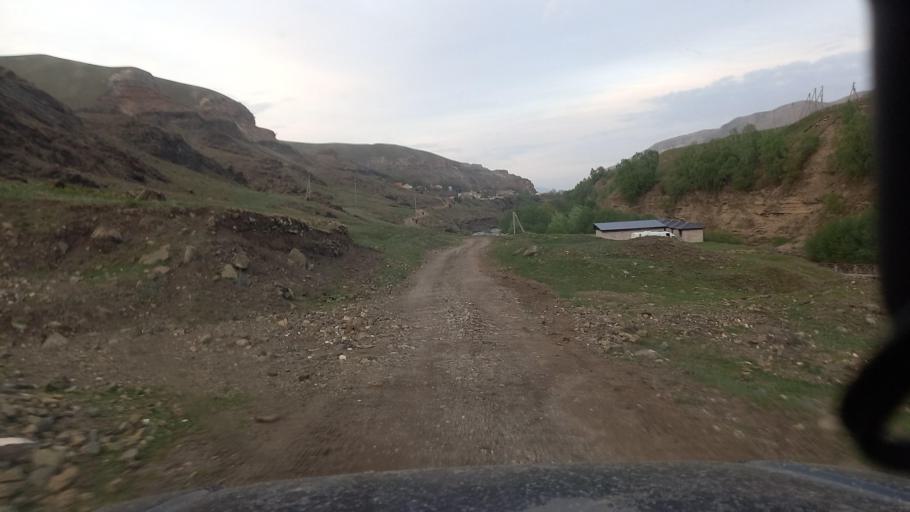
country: RU
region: Kabardino-Balkariya
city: Kamennomostskoye
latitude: 43.7238
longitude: 42.9051
